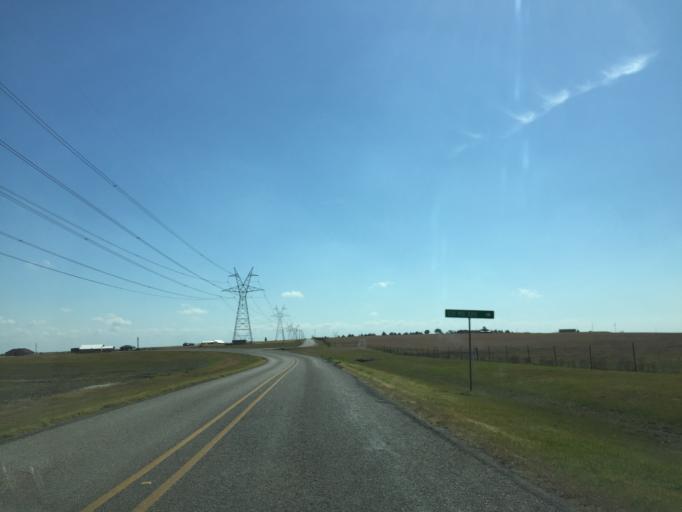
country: US
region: Texas
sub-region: Williamson County
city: Granger
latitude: 30.7555
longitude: -97.5235
